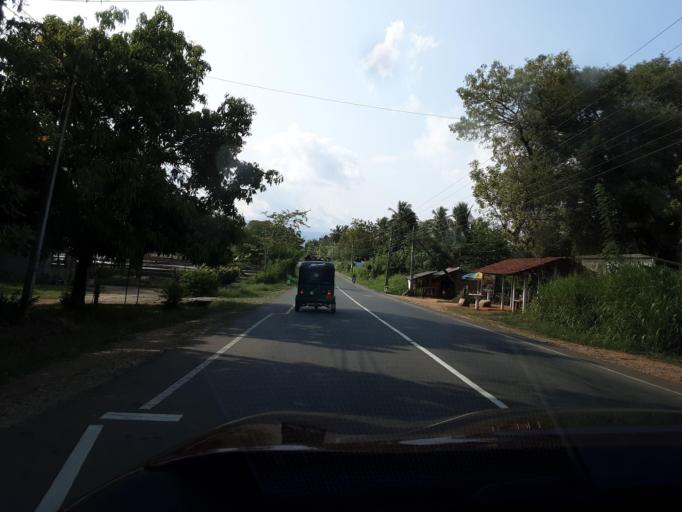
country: LK
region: Uva
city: Haputale
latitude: 6.5969
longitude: 81.1418
